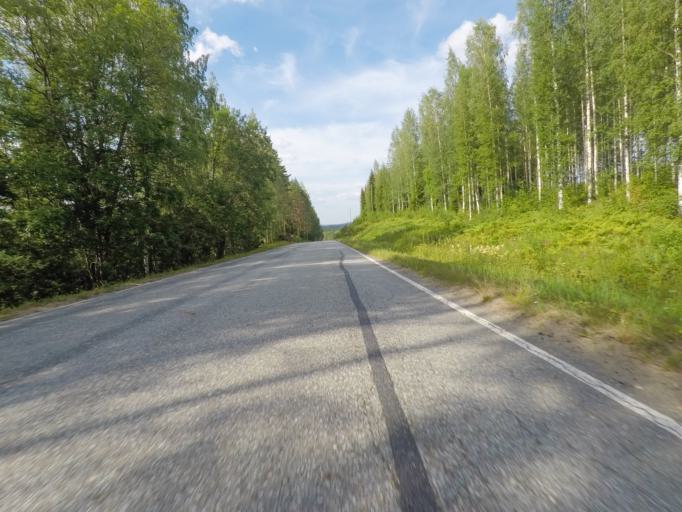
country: FI
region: Southern Savonia
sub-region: Savonlinna
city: Sulkava
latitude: 61.7114
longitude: 28.2103
